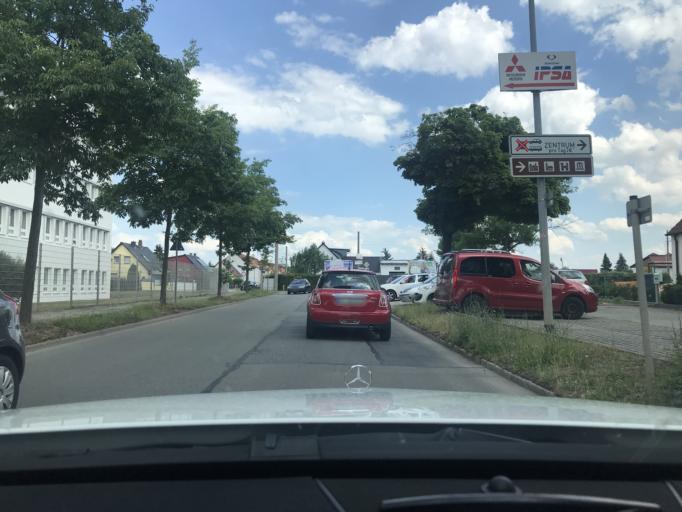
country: DE
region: Thuringia
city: Arnstadt
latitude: 50.8455
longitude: 10.9608
